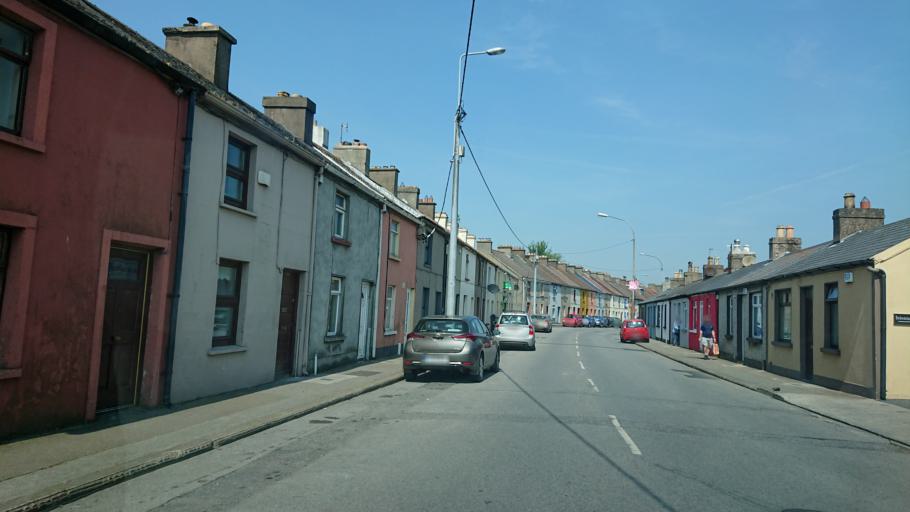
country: IE
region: Munster
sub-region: Waterford
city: Waterford
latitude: 52.2515
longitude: -7.1114
